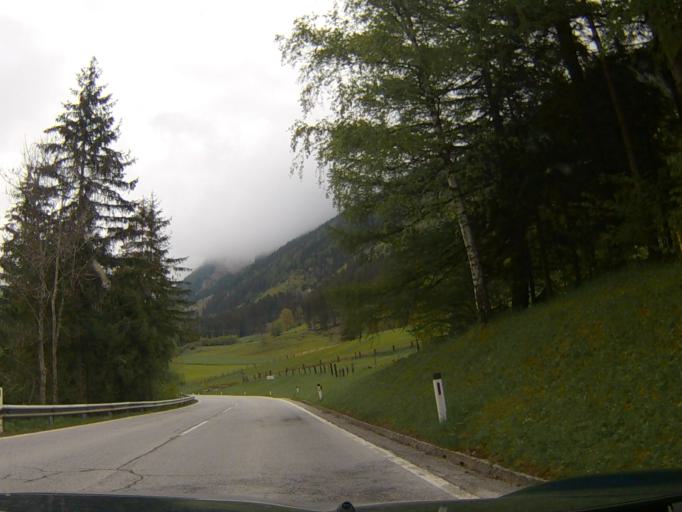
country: AT
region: Carinthia
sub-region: Politischer Bezirk Spittal an der Drau
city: Obervellach
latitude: 46.9547
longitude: 13.1840
